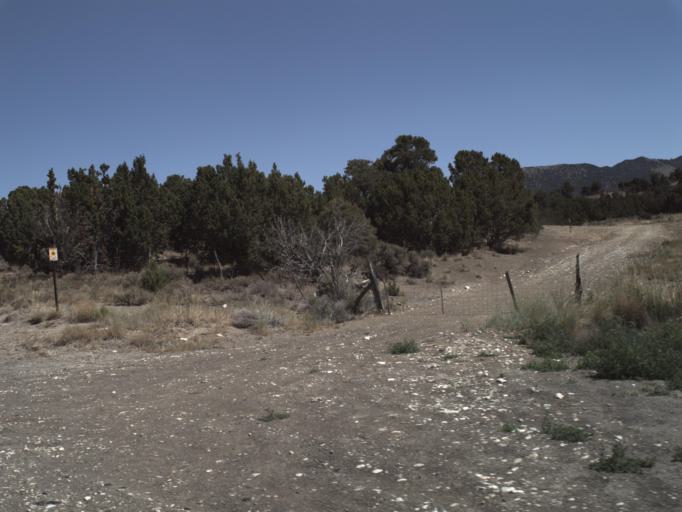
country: US
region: Utah
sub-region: Utah County
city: Genola
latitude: 39.9546
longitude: -112.2405
